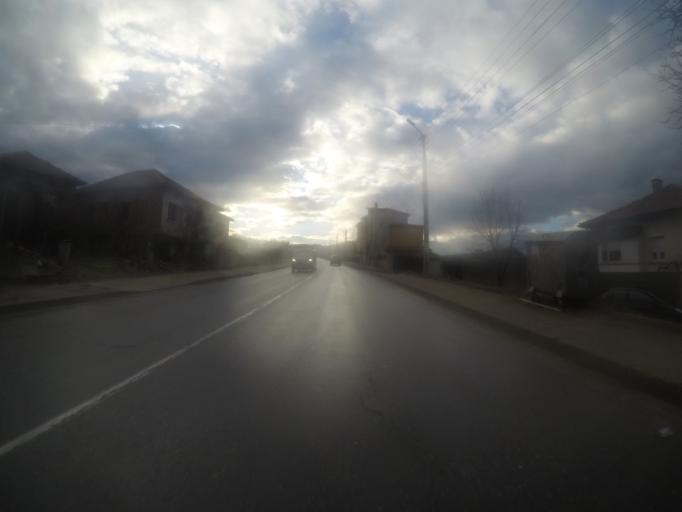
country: BG
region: Blagoevgrad
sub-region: Obshtina Simitli
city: Simitli
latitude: 41.8876
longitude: 23.1186
